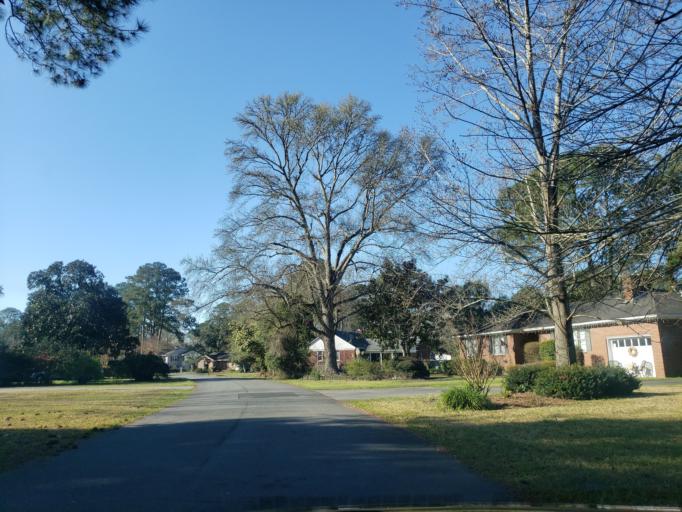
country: US
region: Georgia
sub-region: Chatham County
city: Thunderbolt
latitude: 32.0223
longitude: -81.0941
